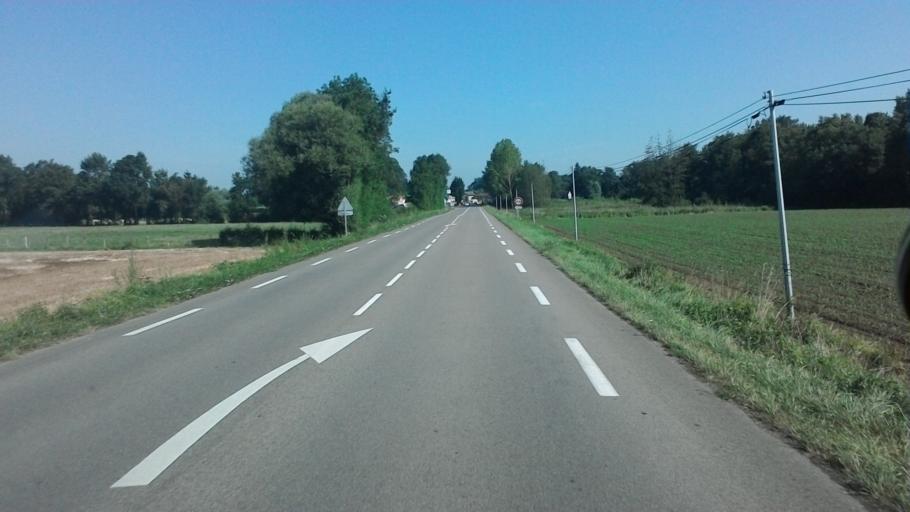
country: FR
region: Rhone-Alpes
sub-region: Departement de l'Ain
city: Montrevel-en-Bresse
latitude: 46.3956
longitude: 5.1143
